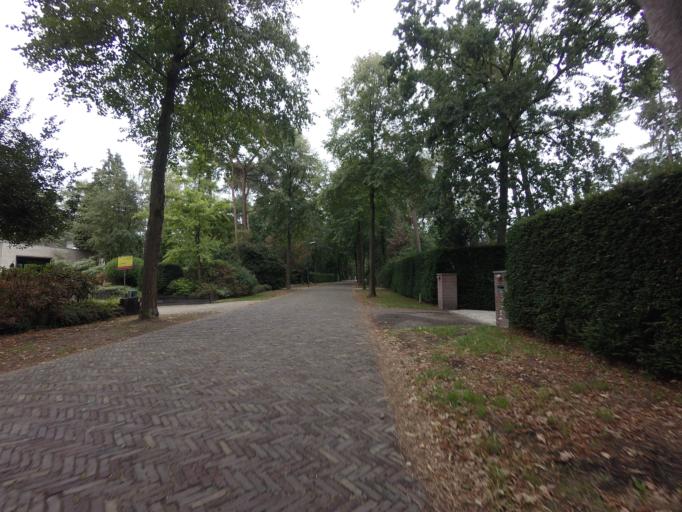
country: NL
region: Utrecht
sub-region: Gemeente Zeist
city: Zeist
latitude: 52.1451
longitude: 5.2262
